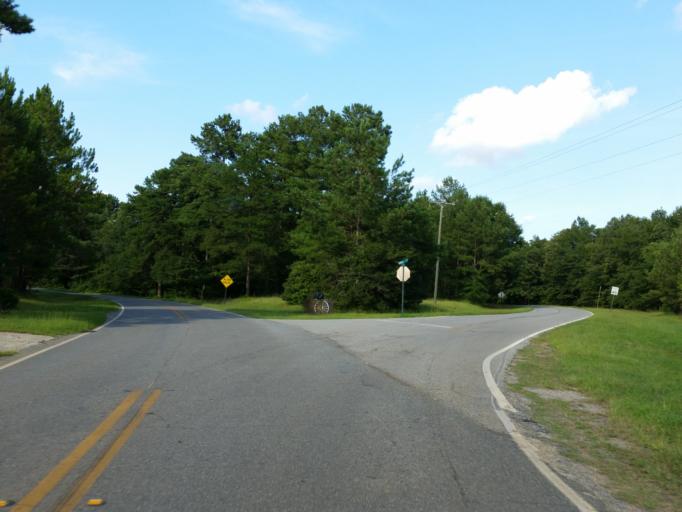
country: US
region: Georgia
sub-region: Lee County
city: Leesburg
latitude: 31.9049
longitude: -84.0364
